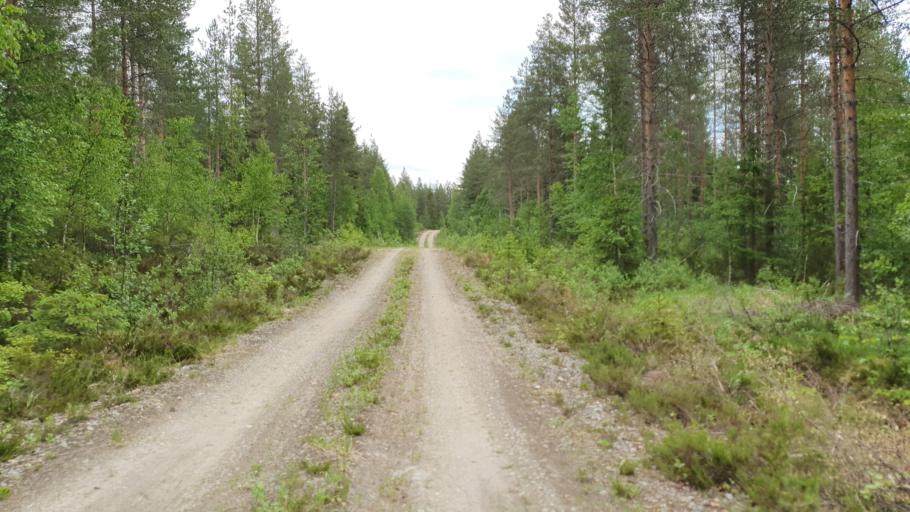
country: FI
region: Kainuu
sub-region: Kehys-Kainuu
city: Kuhmo
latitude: 64.4406
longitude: 29.6929
